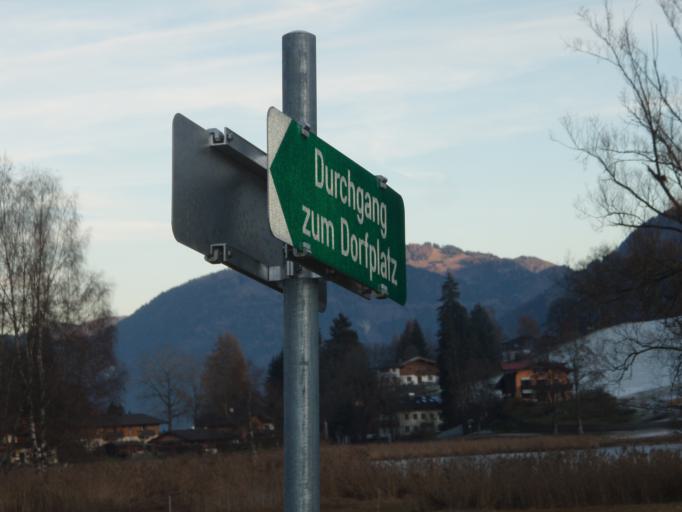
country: AT
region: Salzburg
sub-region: Politischer Bezirk Sankt Johann im Pongau
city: Goldegg
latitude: 47.3183
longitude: 13.1003
